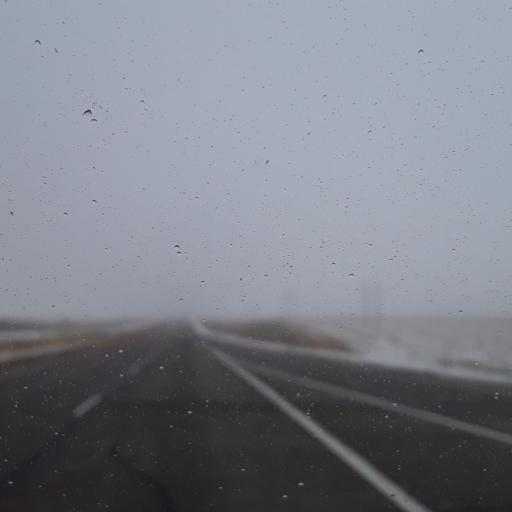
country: US
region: Colorado
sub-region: Logan County
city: Sterling
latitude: 40.7705
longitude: -102.9384
